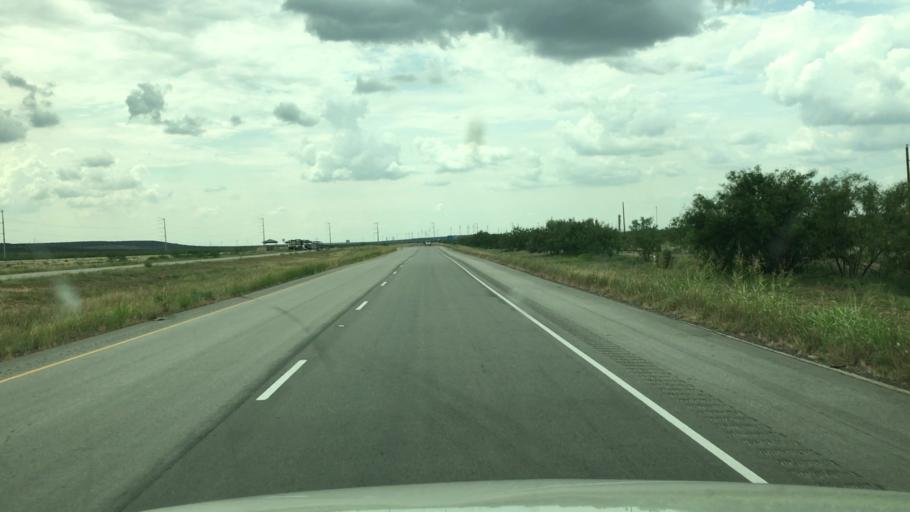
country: US
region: Texas
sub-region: Sterling County
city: Sterling City
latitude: 31.9646
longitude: -101.2255
